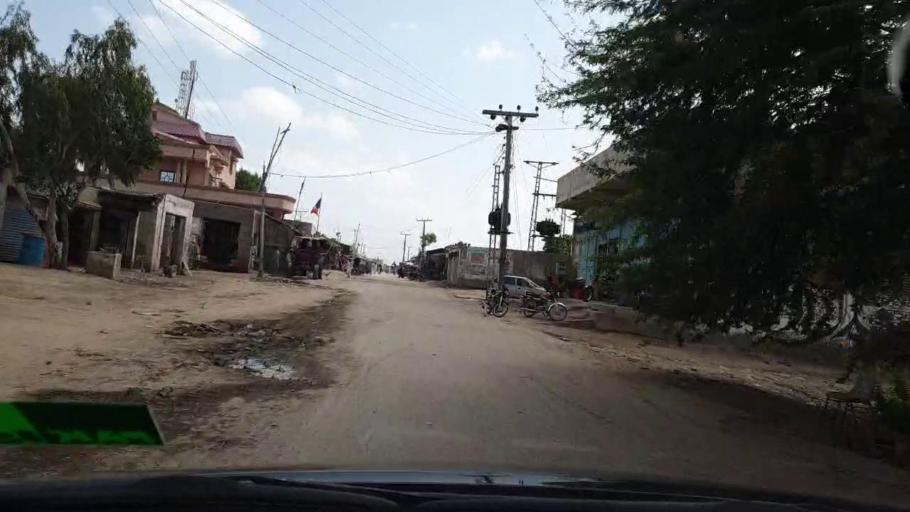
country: PK
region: Sindh
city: Kadhan
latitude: 24.6276
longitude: 69.1773
